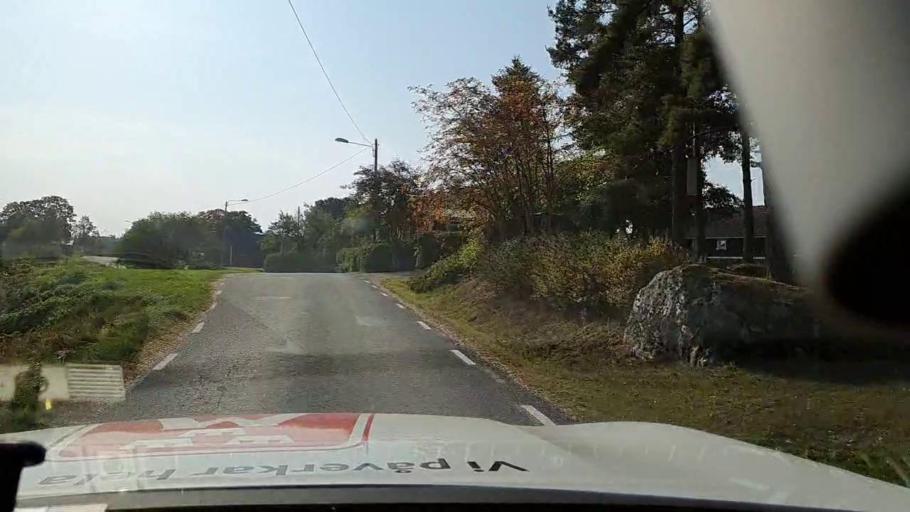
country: SE
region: Soedermanland
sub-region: Eskilstuna Kommun
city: Kvicksund
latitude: 59.3173
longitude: 16.2476
